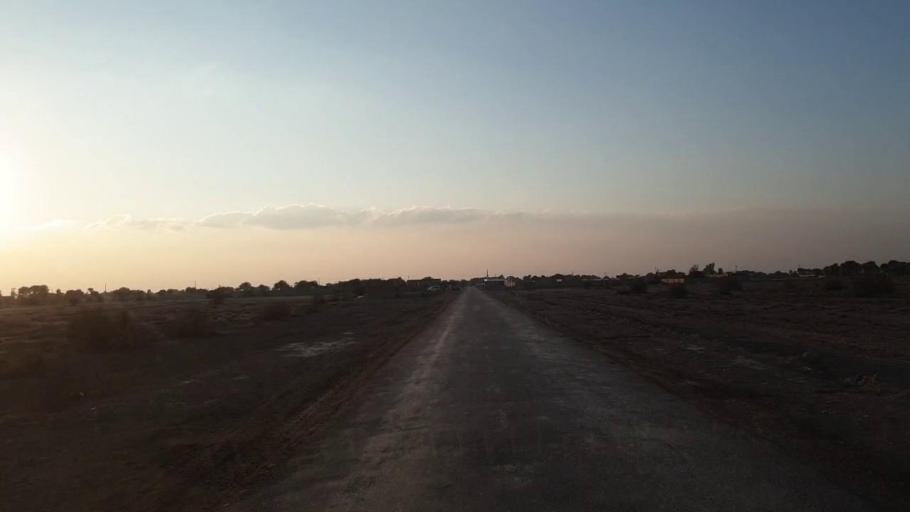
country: PK
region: Sindh
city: Shahpur Chakar
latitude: 26.1575
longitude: 68.5474
